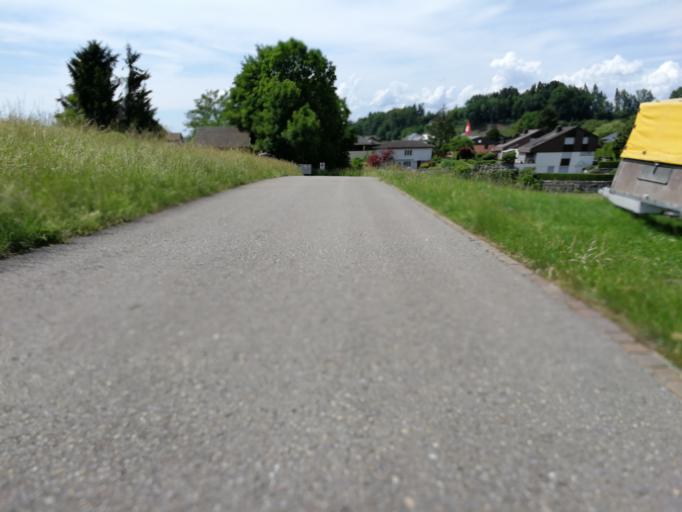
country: CH
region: Saint Gallen
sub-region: Wahlkreis See-Gaster
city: Rapperswil
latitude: 47.2438
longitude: 8.8232
